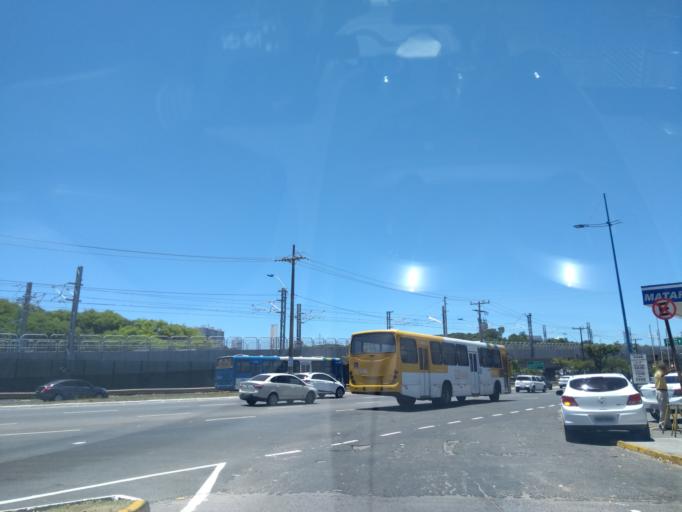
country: BR
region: Bahia
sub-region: Salvador
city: Salvador
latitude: -12.9789
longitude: -38.4671
